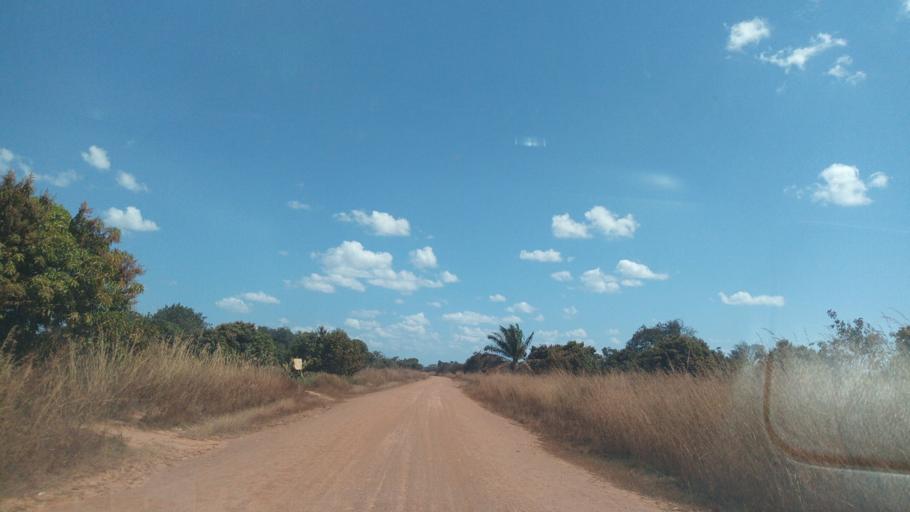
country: ZM
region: Luapula
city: Mwense
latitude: -10.7497
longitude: 28.2715
